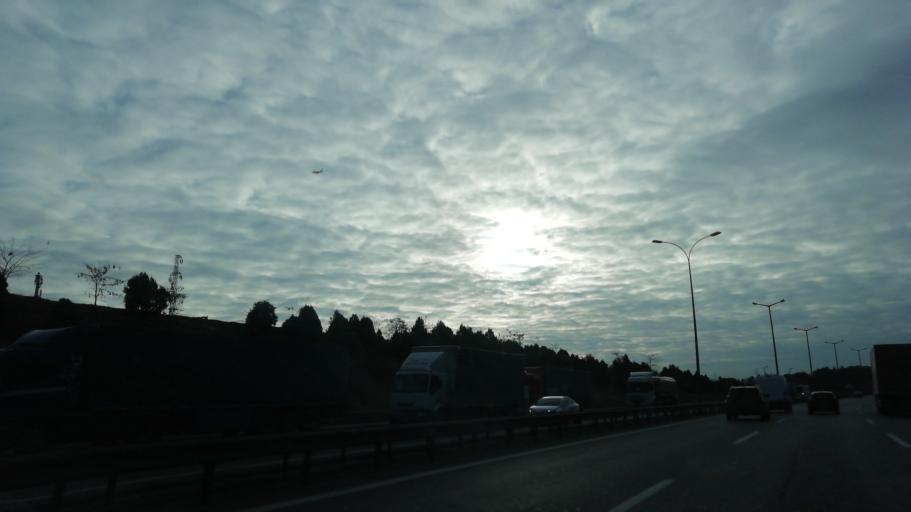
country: TR
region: Istanbul
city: Sultanbeyli
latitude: 40.9263
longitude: 29.3495
